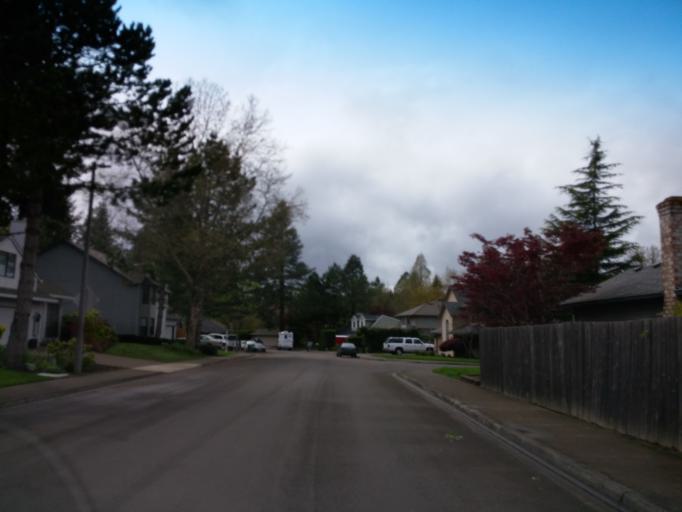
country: US
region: Oregon
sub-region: Washington County
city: Cedar Mill
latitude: 45.5186
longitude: -122.8288
